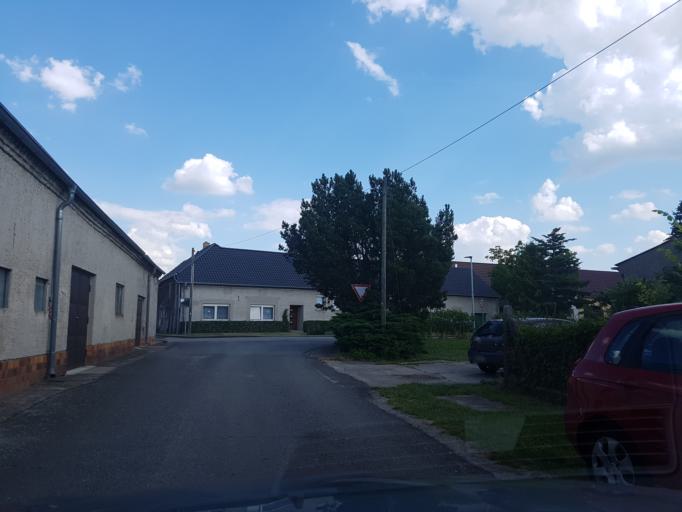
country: DE
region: Brandenburg
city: Schlieben
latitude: 51.6890
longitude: 13.3546
